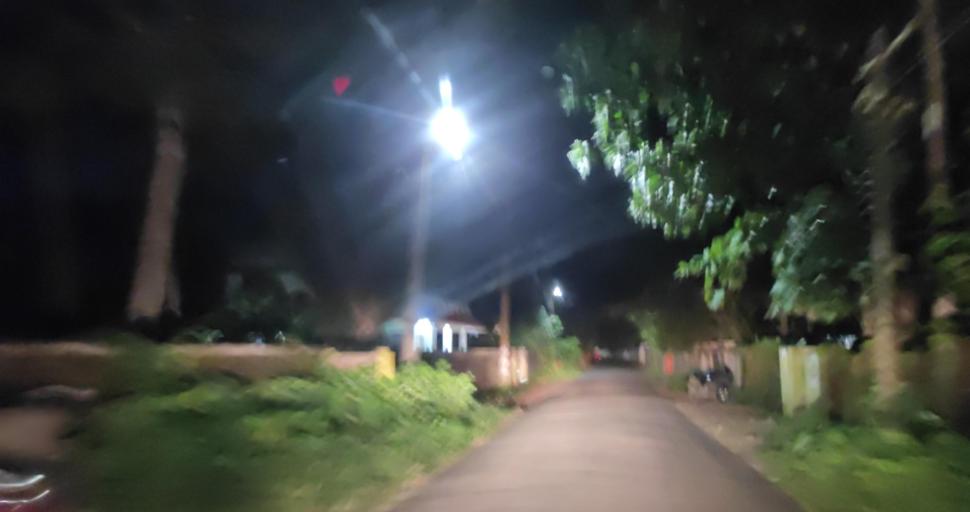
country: IN
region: Kerala
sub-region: Alappuzha
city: Vayalar
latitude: 9.6806
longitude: 76.3167
